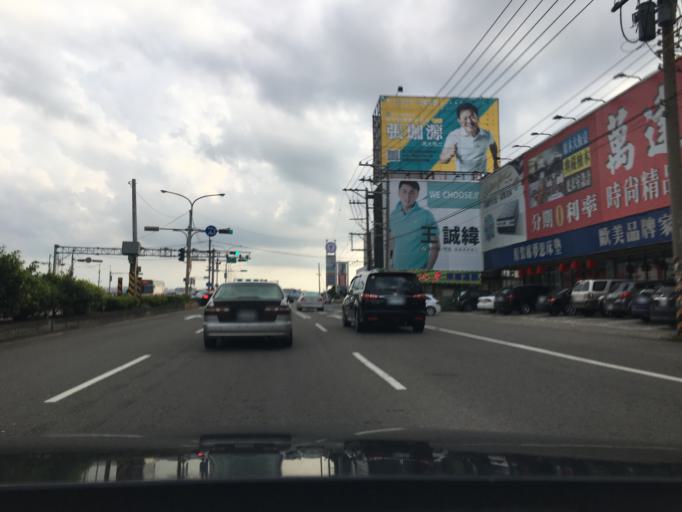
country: TW
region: Taiwan
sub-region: Hsinchu
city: Zhubei
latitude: 24.8265
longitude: 120.9976
